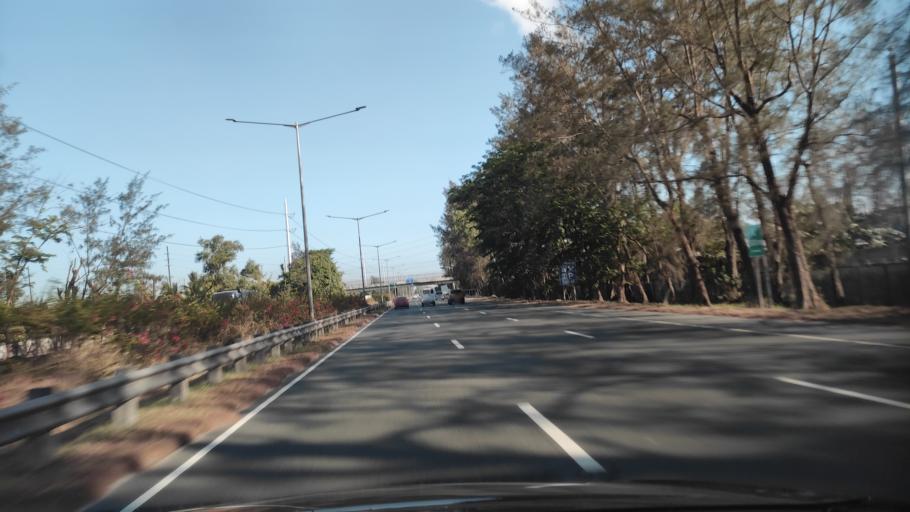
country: PH
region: Central Luzon
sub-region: Province of Bulacan
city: Plaridel
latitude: 14.8806
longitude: 120.8387
